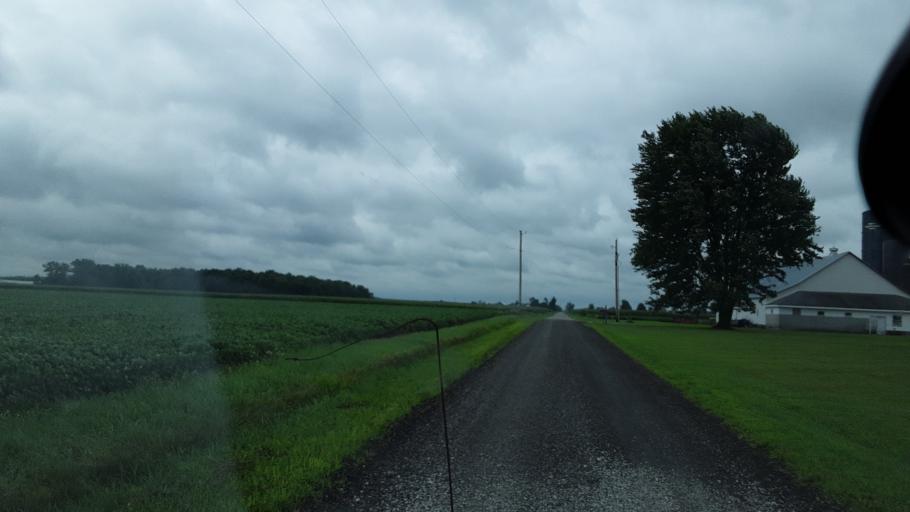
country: US
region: Indiana
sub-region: Wells County
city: Ossian
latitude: 40.8506
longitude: -85.0819
